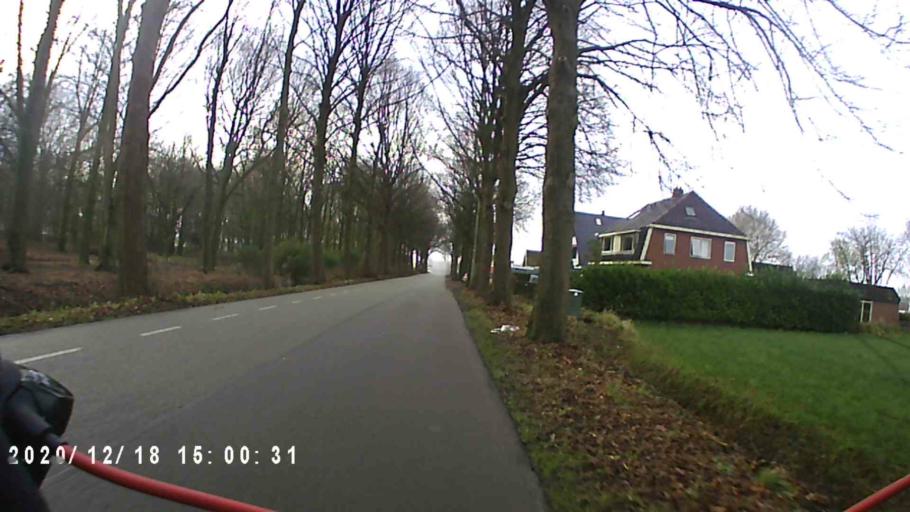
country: NL
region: Groningen
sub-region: Gemeente Haren
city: Haren
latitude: 53.1797
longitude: 6.6849
